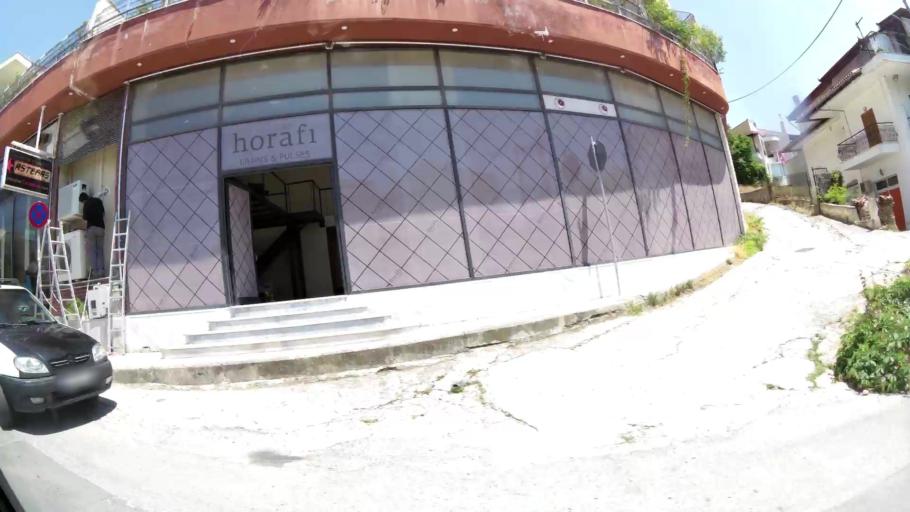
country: GR
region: Central Macedonia
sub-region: Nomos Thessalonikis
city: Trilofos
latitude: 40.4704
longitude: 22.9696
